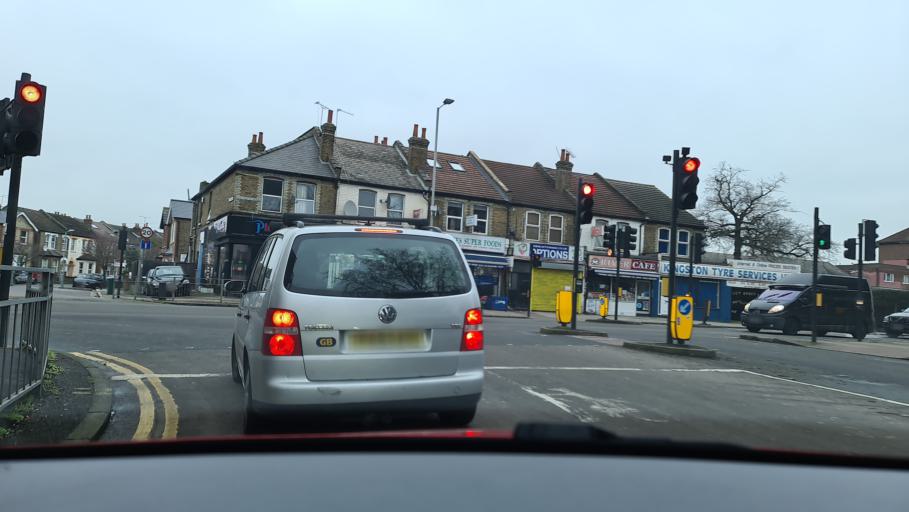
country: GB
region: England
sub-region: Greater London
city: Kingston upon Thames
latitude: 51.4096
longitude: -0.2896
